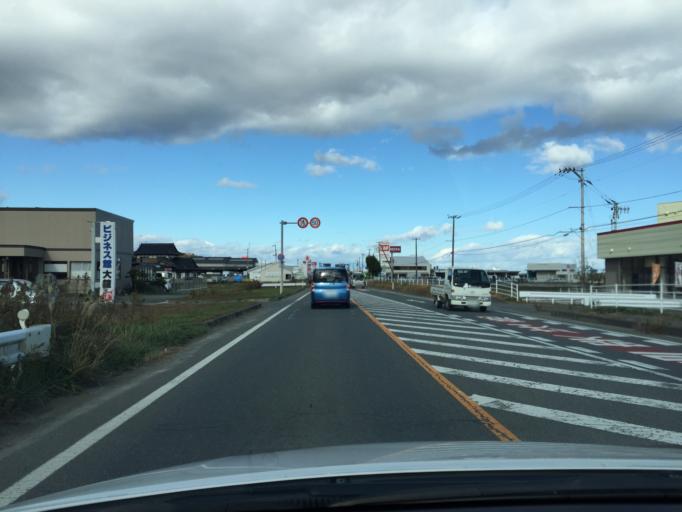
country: JP
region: Fukushima
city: Namie
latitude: 37.6135
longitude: 141.0039
